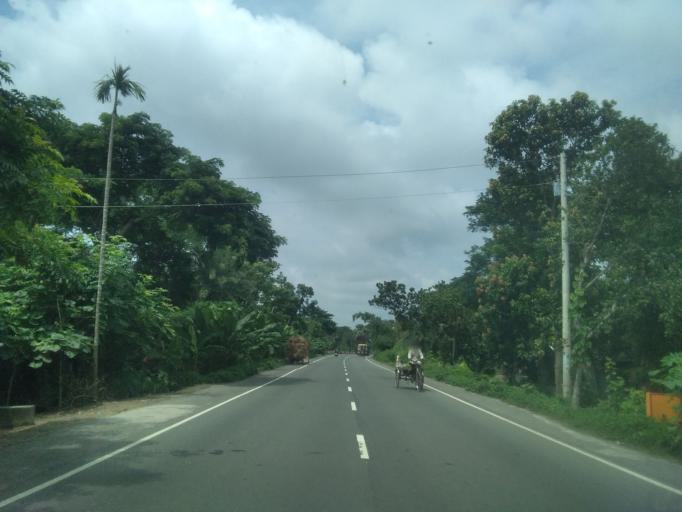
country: BD
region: Khulna
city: Kesabpur
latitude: 22.8182
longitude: 89.2605
